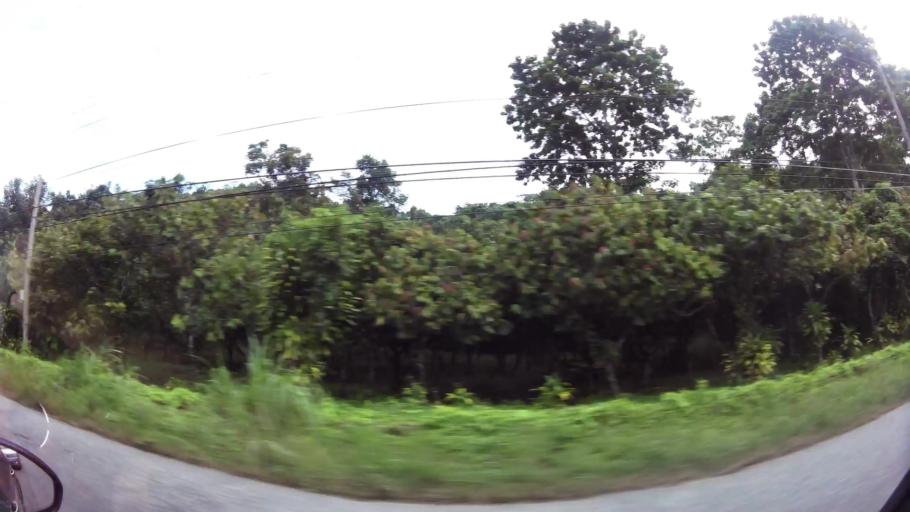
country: TT
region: San Juan/Laventille
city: Laventille
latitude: 10.7008
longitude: -61.4585
